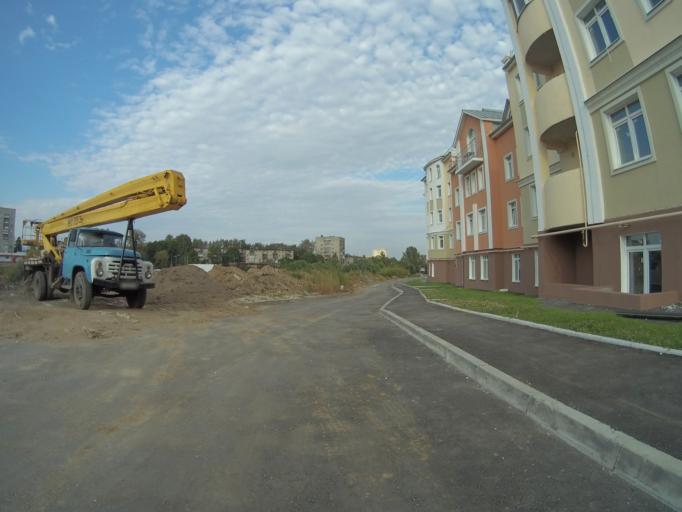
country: RU
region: Vladimir
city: Vladimir
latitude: 56.1371
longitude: 40.4254
